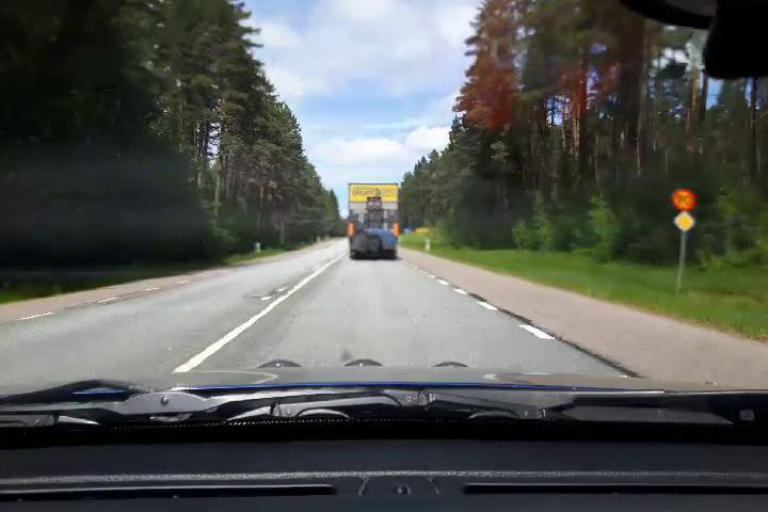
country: SE
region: Uppsala
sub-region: Tierps Kommun
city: Tierp
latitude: 60.2021
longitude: 17.4820
